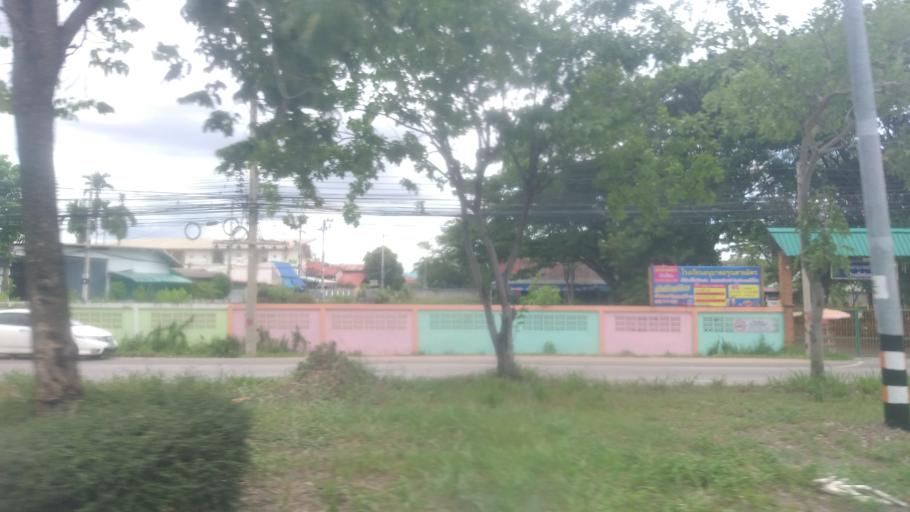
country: TH
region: Nakhon Ratchasima
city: Nakhon Ratchasima
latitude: 15.0413
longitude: 102.1352
